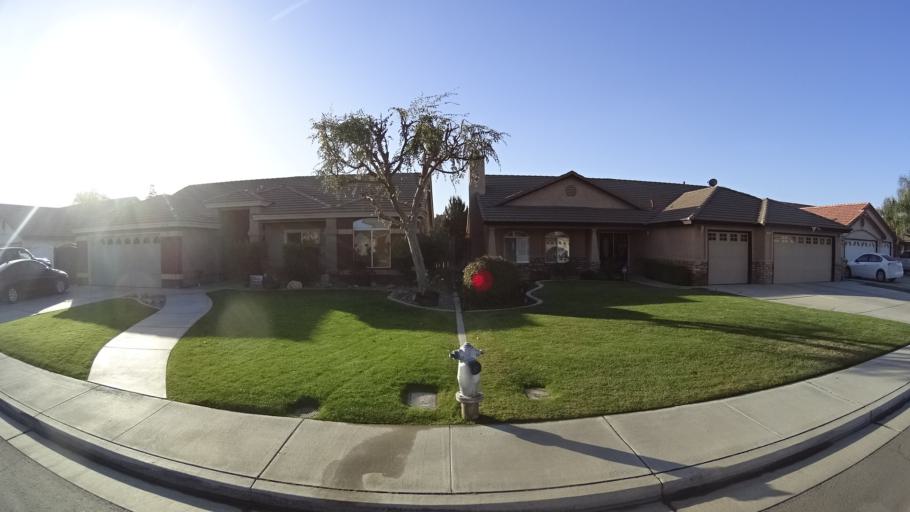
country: US
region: California
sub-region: Kern County
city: Greenfield
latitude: 35.2773
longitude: -119.0379
